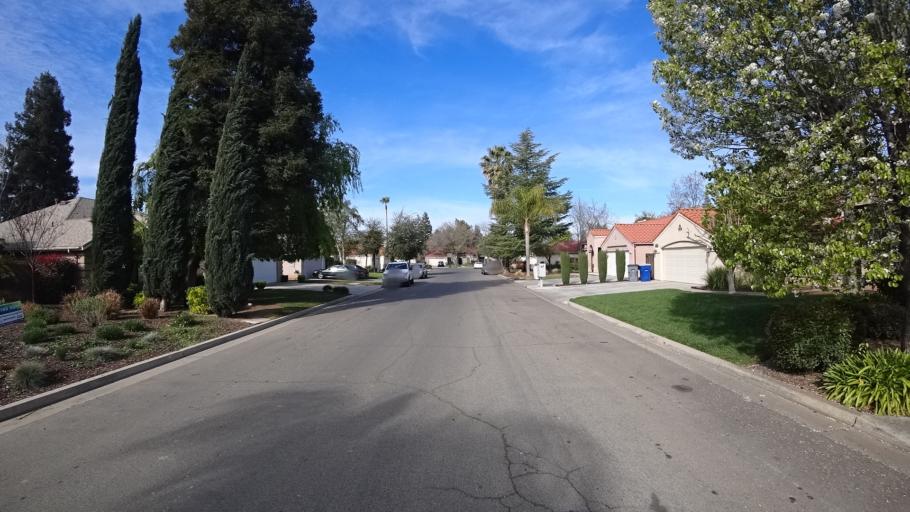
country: US
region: California
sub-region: Fresno County
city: West Park
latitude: 36.8306
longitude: -119.8677
